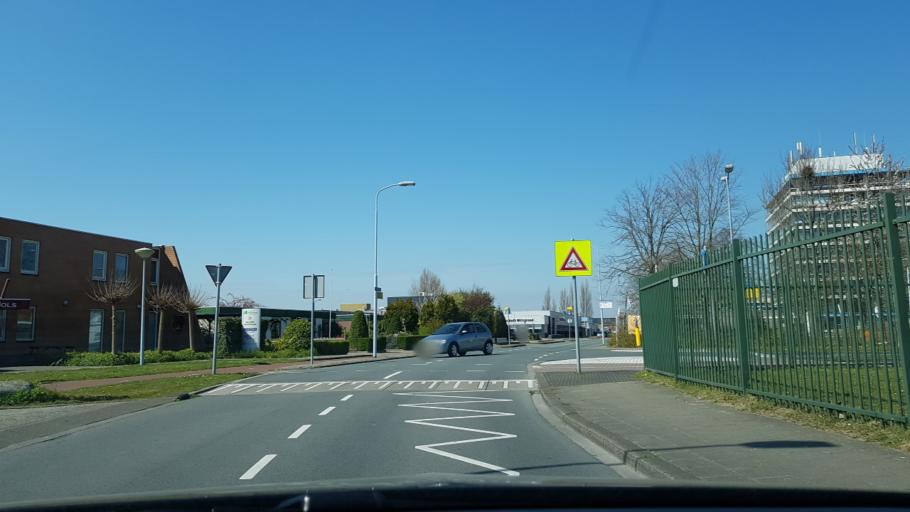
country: NL
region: South Holland
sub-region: Gemeente Hillegom
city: Hillegom
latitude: 52.2723
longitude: 4.6307
